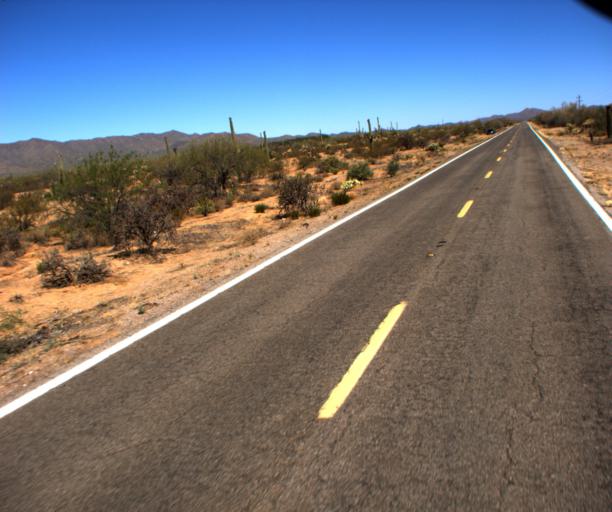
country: US
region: Arizona
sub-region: Pima County
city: Sells
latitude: 32.1037
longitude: -112.0684
